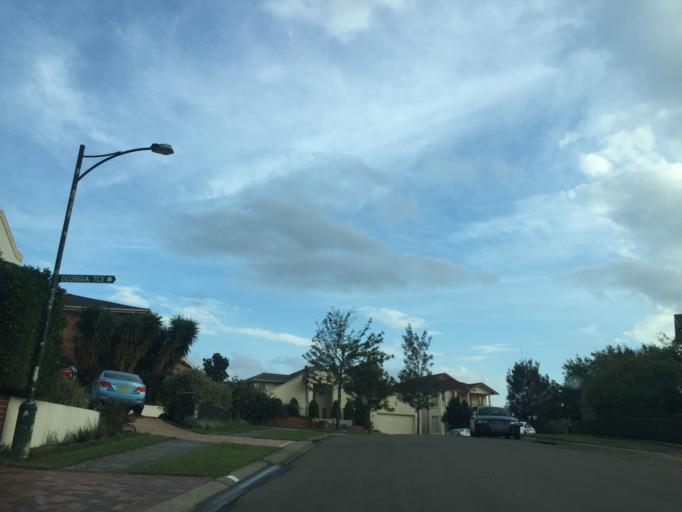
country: AU
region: New South Wales
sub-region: The Hills Shire
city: Glenhaven
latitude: -33.6998
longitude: 150.9744
